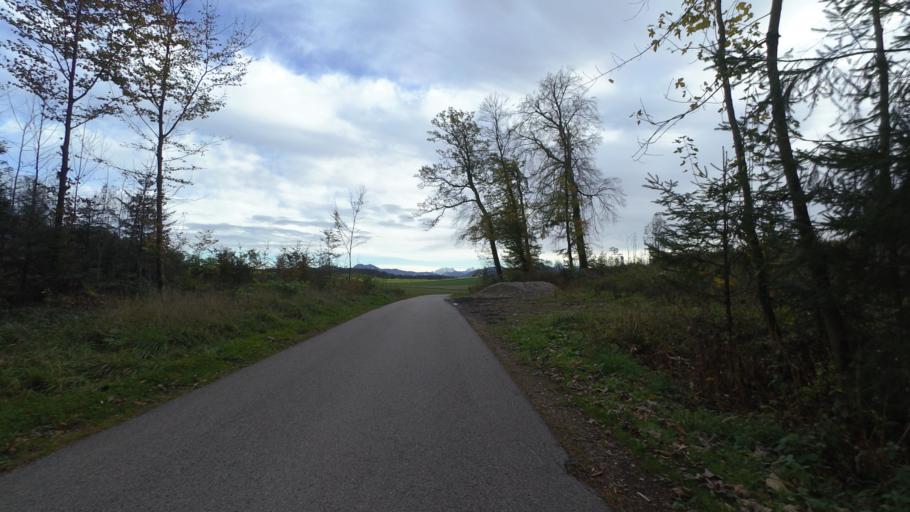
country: DE
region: Bavaria
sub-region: Upper Bavaria
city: Nussdorf
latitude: 47.9125
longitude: 12.5940
